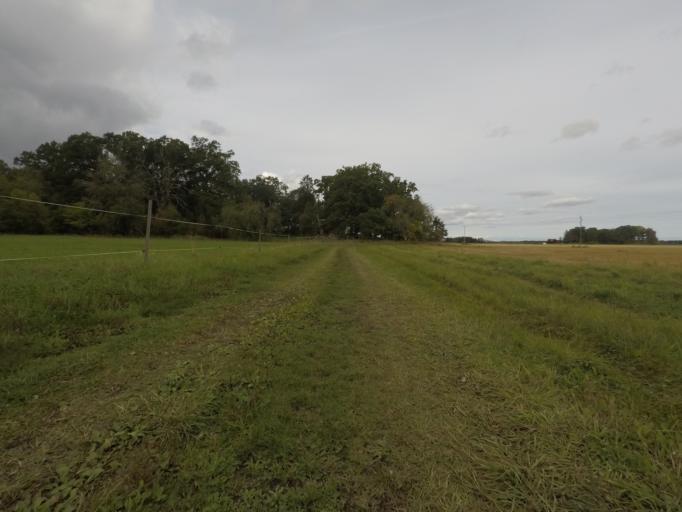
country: SE
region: Vaestmanland
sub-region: Kungsors Kommun
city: Kungsoer
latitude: 59.4548
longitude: 16.0503
